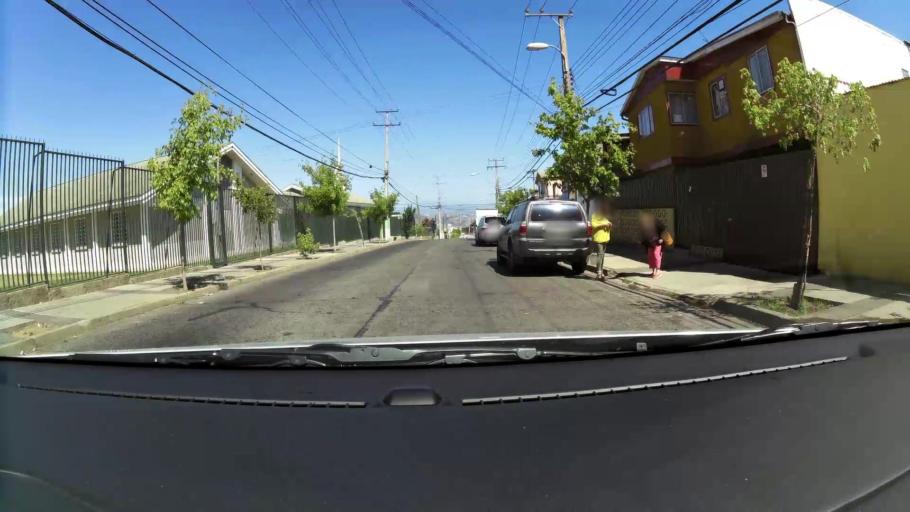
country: CL
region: Valparaiso
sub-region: Provincia de Valparaiso
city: Vina del Mar
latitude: -33.0531
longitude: -71.5811
